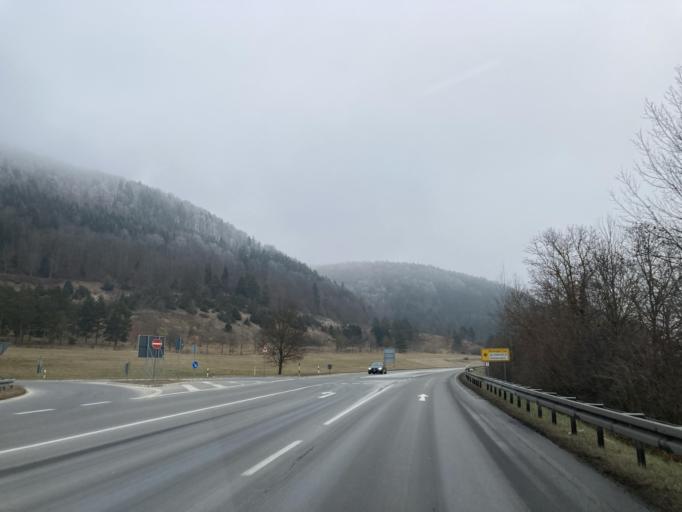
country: DE
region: Baden-Wuerttemberg
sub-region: Freiburg Region
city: Geisingen
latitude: 47.9253
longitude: 8.6769
